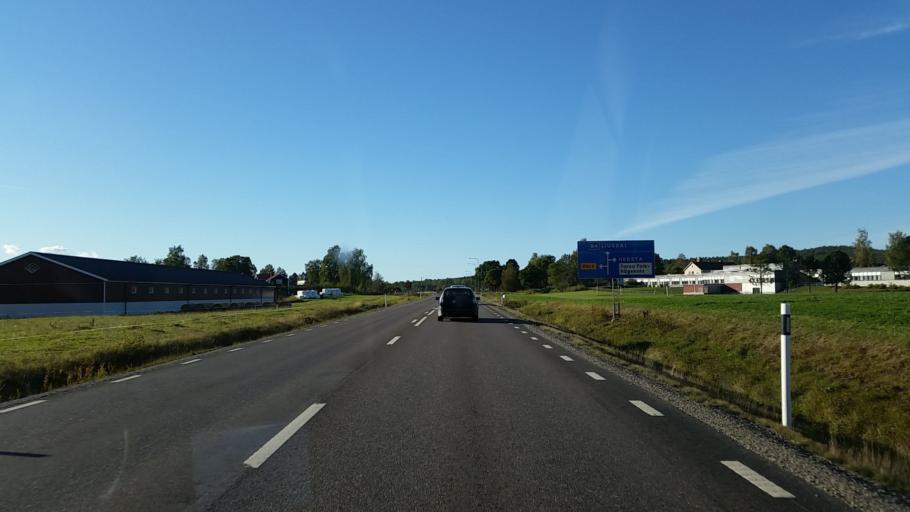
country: SE
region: Gaevleborg
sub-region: Hudiksvalls Kommun
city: Sorforsa
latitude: 61.7270
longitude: 16.9697
